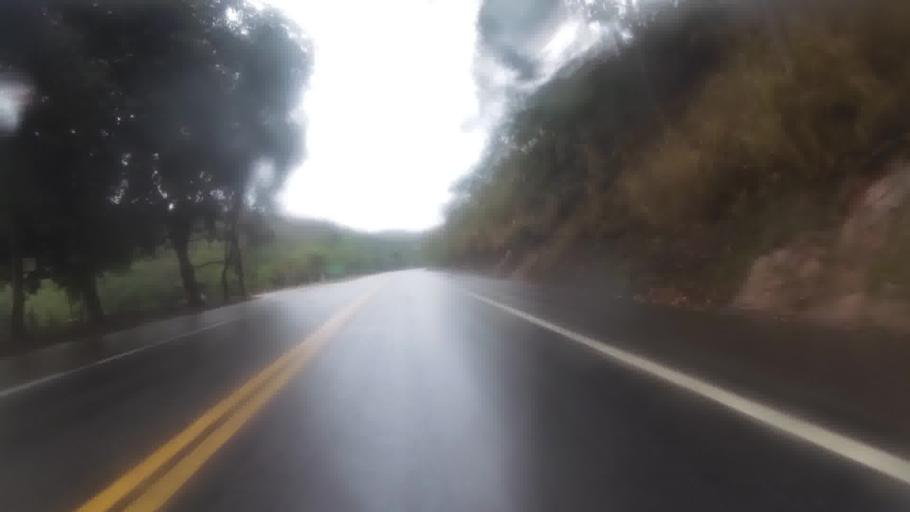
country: BR
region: Espirito Santo
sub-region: Cachoeiro De Itapemirim
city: Cachoeiro de Itapemirim
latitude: -21.0235
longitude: -41.1574
